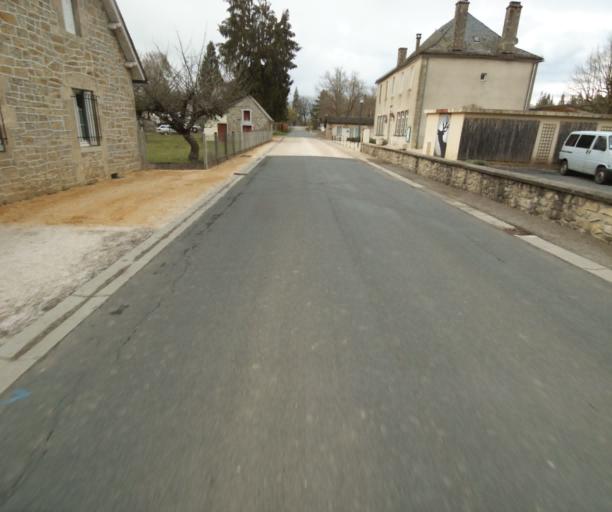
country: FR
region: Limousin
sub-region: Departement de la Correze
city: Saint-Privat
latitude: 45.2149
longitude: 2.0036
